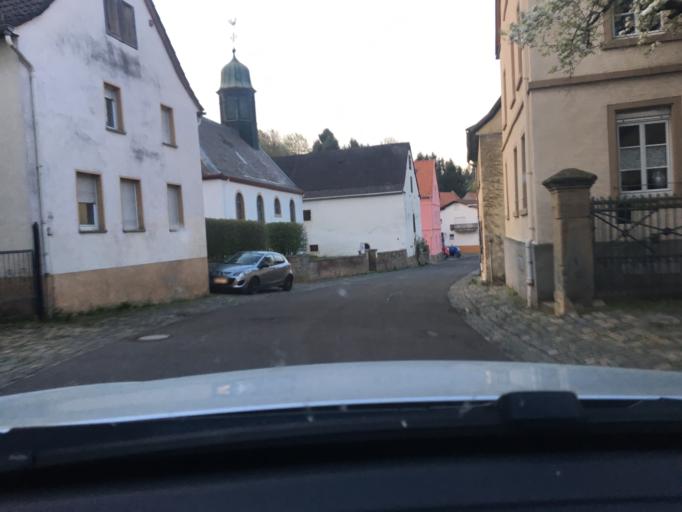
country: DE
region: Rheinland-Pfalz
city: Kalkofen
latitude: 49.7323
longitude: 7.8353
